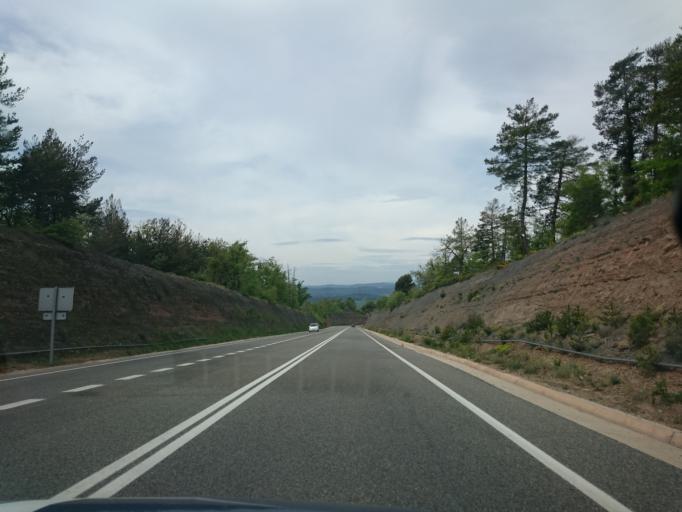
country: ES
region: Catalonia
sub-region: Provincia de Barcelona
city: Olost
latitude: 41.9726
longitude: 2.1229
